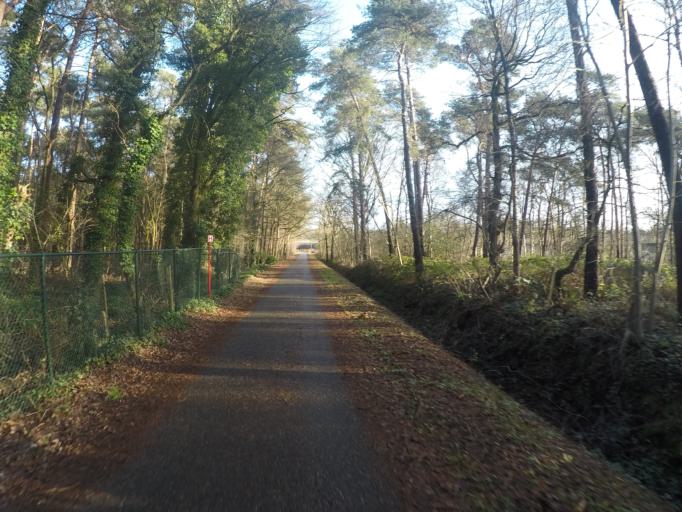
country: BE
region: Flanders
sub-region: Provincie Antwerpen
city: Brecht
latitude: 51.3294
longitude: 4.5961
